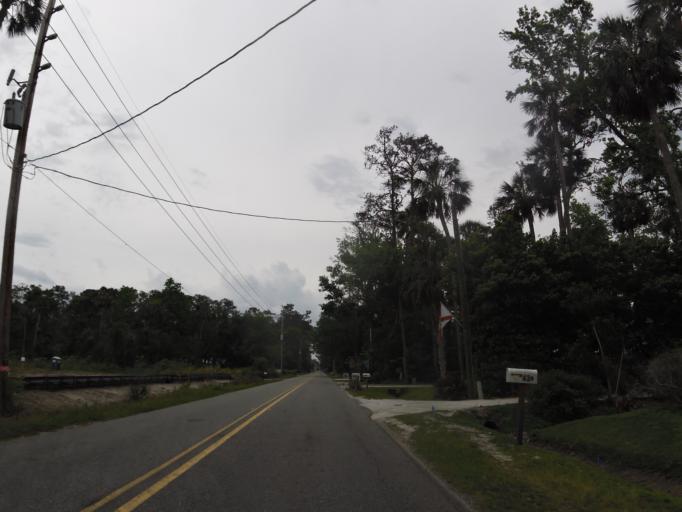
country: US
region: Florida
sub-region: Saint Johns County
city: Palm Valley
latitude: 30.1827
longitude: -81.4018
